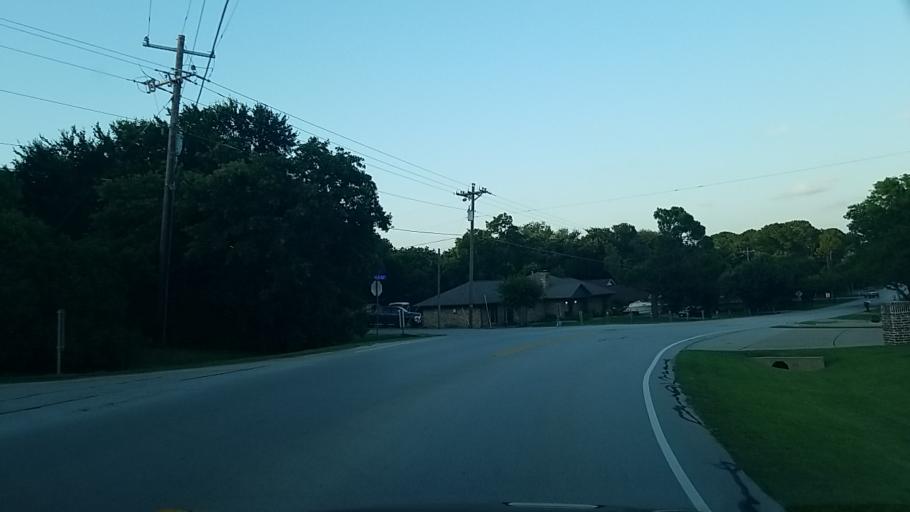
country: US
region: Texas
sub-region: Denton County
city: Highland Village
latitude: 33.0935
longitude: -97.0495
